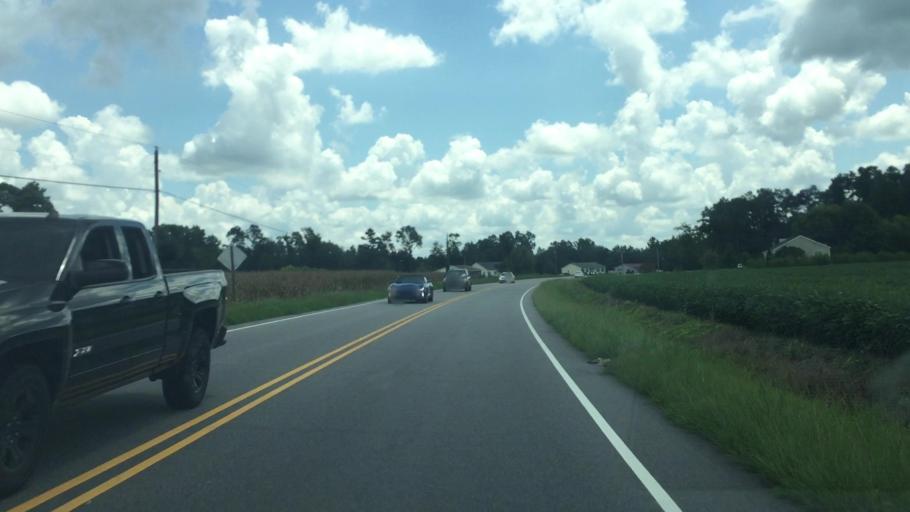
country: US
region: North Carolina
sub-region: Columbus County
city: Chadbourn
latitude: 34.2768
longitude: -78.8141
